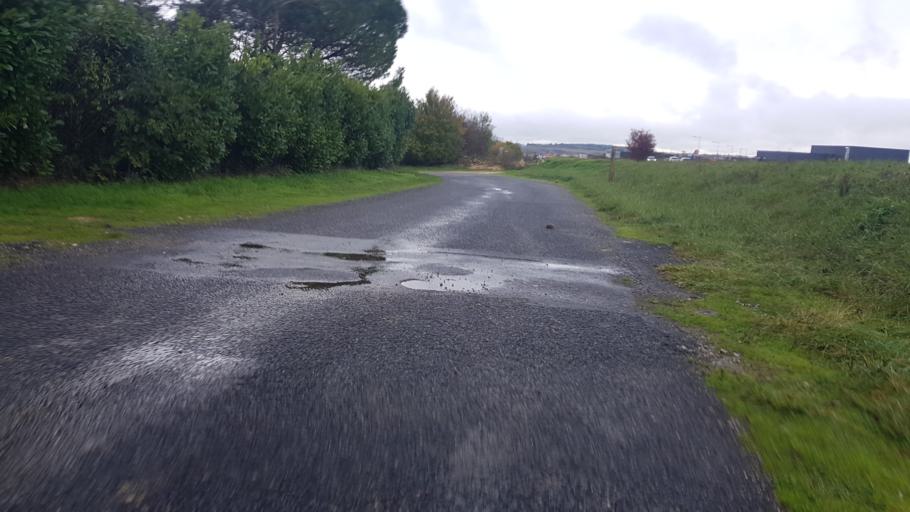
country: FR
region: Poitou-Charentes
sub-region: Departement de la Vienne
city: Chasseneuil-du-Poitou
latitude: 46.6532
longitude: 0.3616
